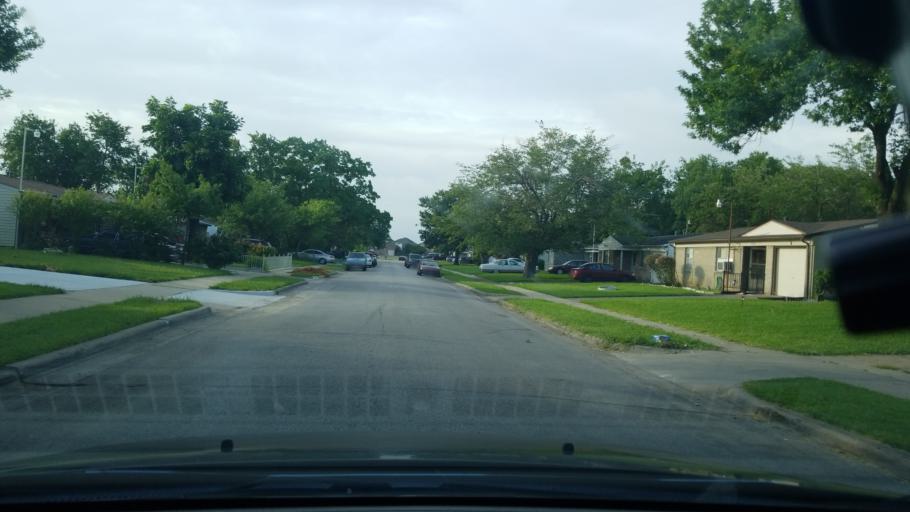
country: US
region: Texas
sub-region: Dallas County
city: Mesquite
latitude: 32.8257
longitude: -96.6513
